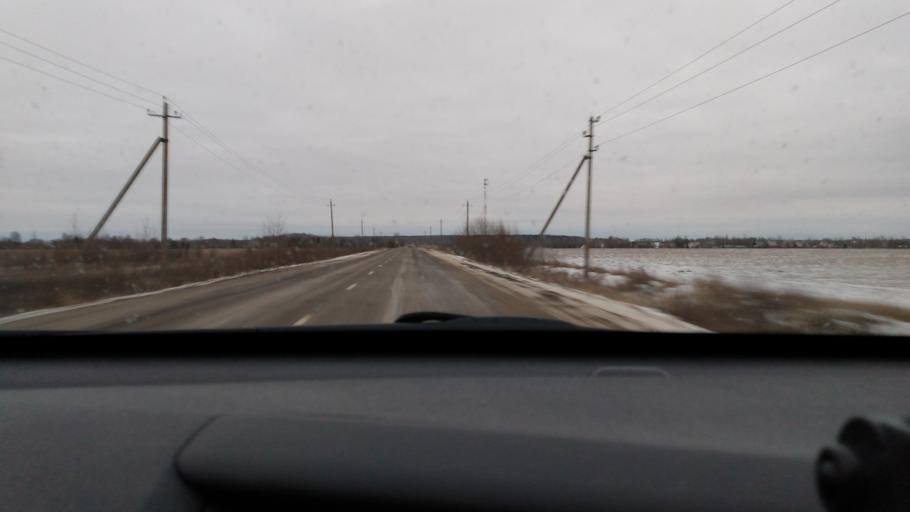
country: RU
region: Moskovskaya
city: Meshcherino
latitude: 55.2907
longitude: 38.3334
